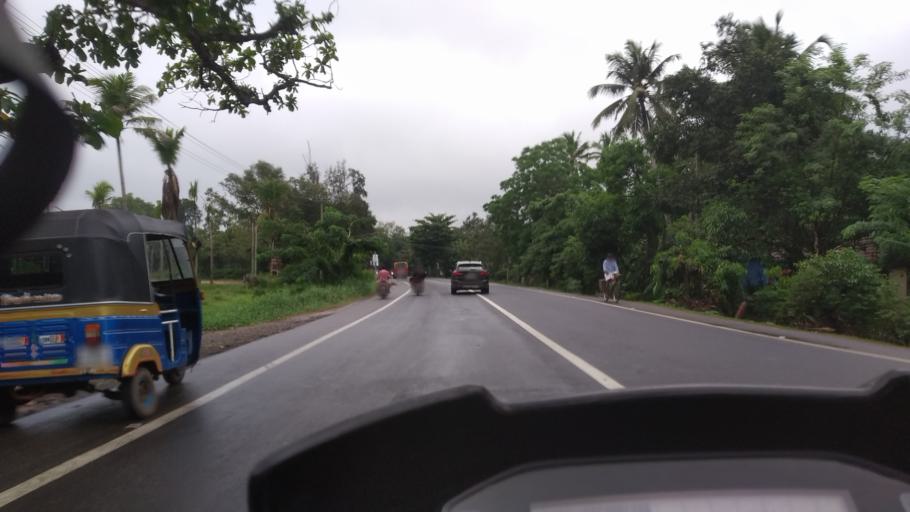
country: IN
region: Kerala
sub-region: Alappuzha
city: Mavelikara
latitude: 9.2980
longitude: 76.4339
